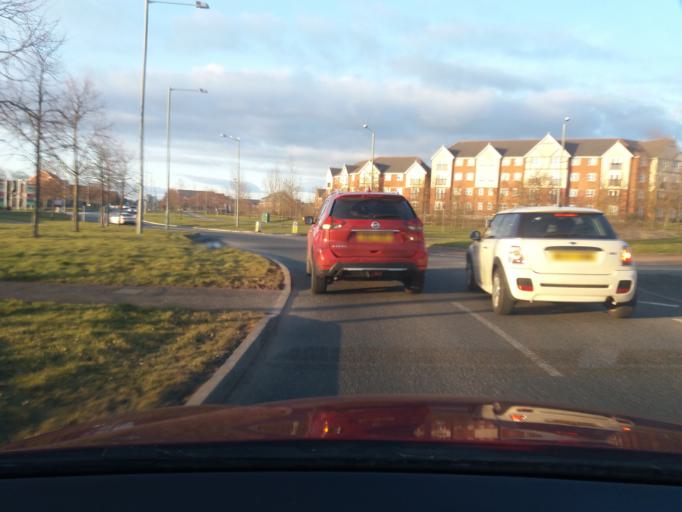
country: GB
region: England
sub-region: Lancashire
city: Euxton
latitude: 53.6766
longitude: -2.6635
